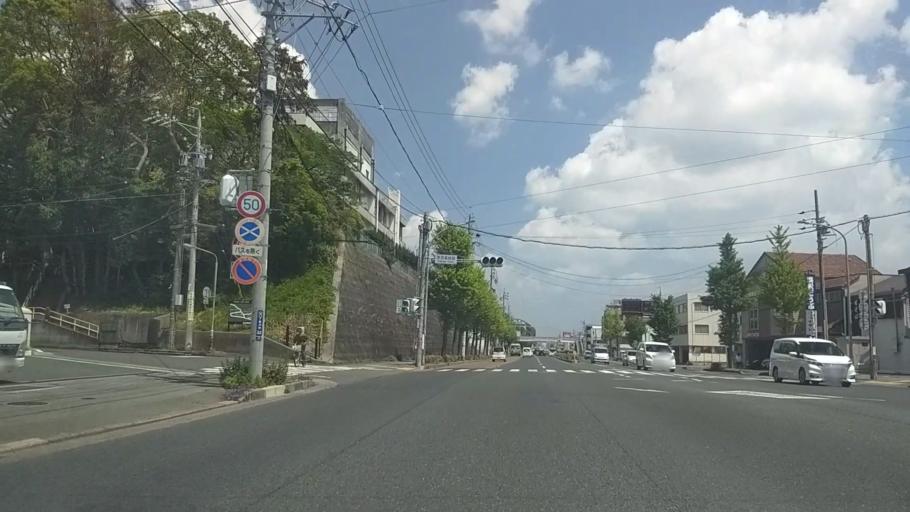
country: JP
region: Shizuoka
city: Hamamatsu
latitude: 34.7184
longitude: 137.7287
